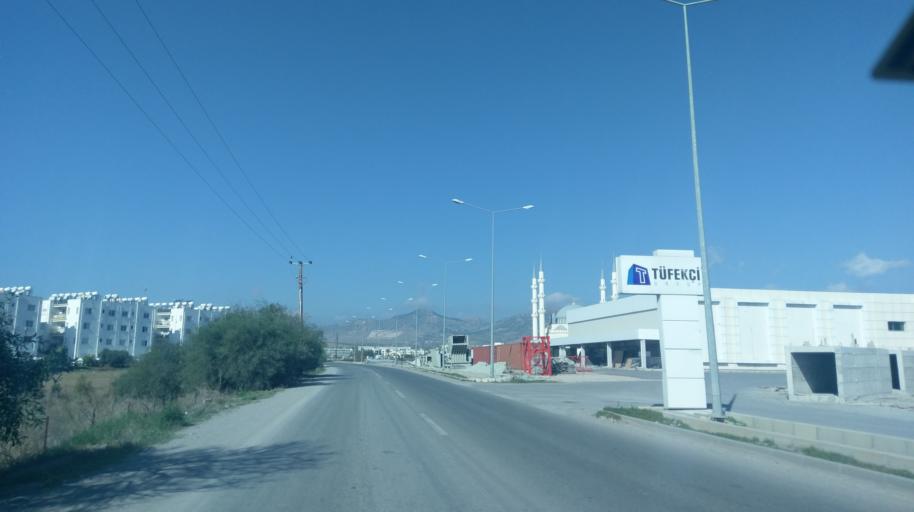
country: CY
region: Lefkosia
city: Nicosia
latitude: 35.2135
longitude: 33.4252
